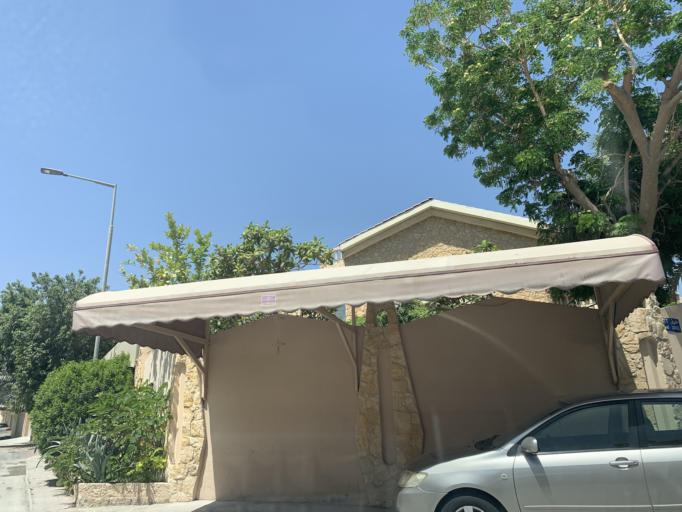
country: BH
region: Northern
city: Ar Rifa'
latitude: 26.1369
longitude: 50.5765
